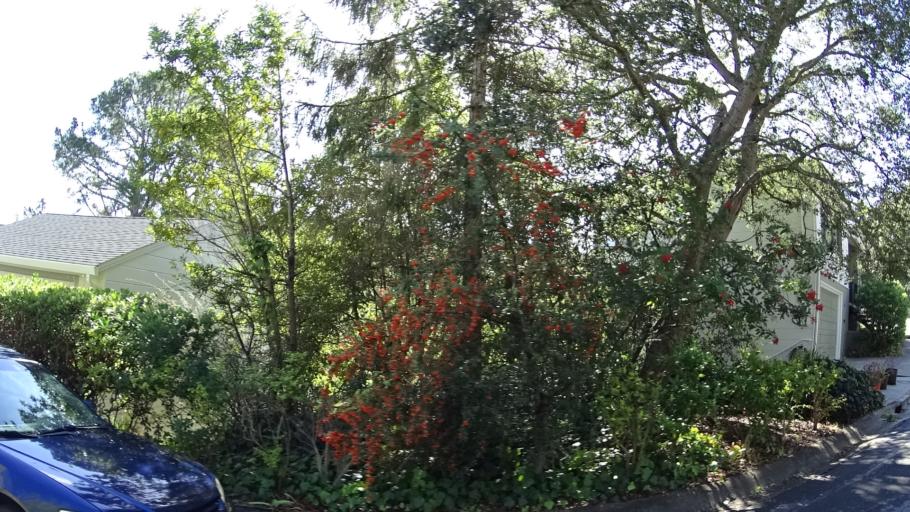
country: US
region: California
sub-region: San Mateo County
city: Millbrae
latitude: 37.5927
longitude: -122.4046
